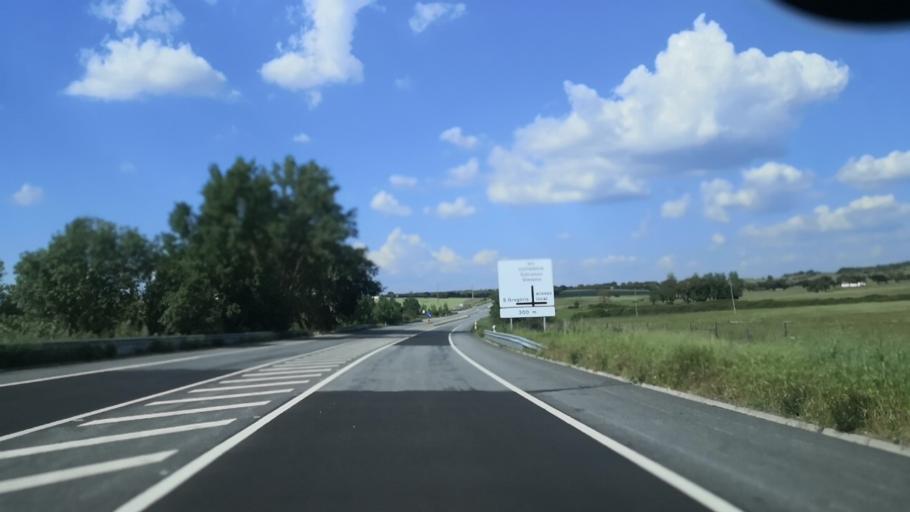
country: PT
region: Evora
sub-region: Arraiolos
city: Arraiolos
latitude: 38.7847
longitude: -7.9054
